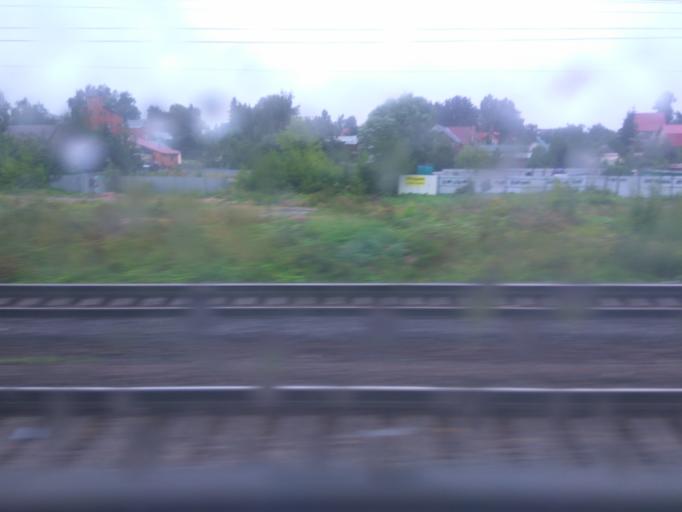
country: RU
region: Moscow
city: Zagor'ye
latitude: 55.5634
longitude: 37.6707
